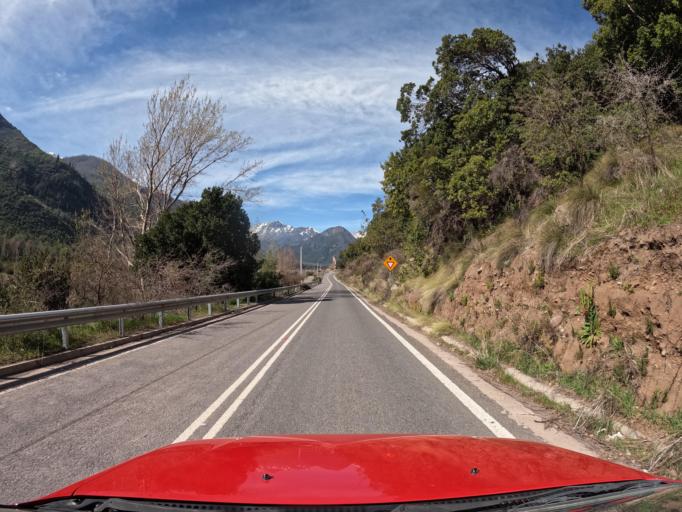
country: CL
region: O'Higgins
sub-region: Provincia de Colchagua
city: Chimbarongo
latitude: -35.0005
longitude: -70.7957
